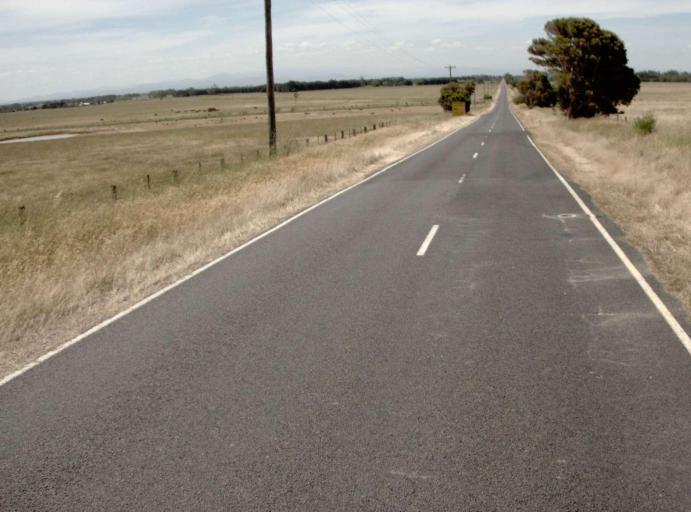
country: AU
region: Victoria
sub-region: Wellington
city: Heyfield
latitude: -38.1125
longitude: 146.8618
